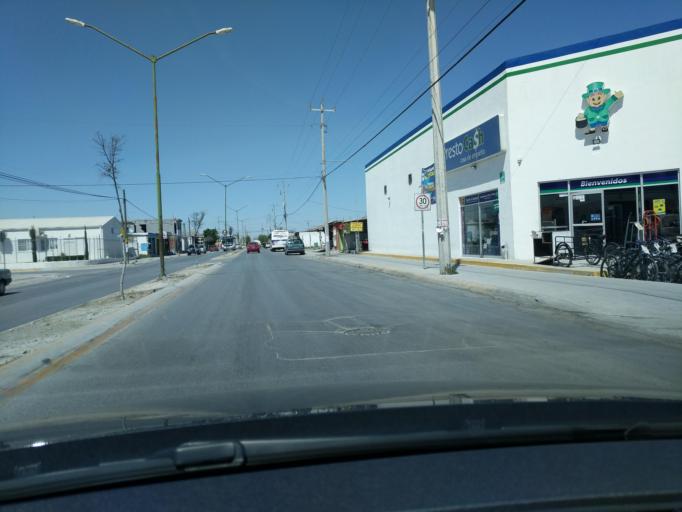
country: MX
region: Nuevo Leon
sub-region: Pesqueria
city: Colinas del Aeropuerto
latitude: 25.8217
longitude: -100.1081
